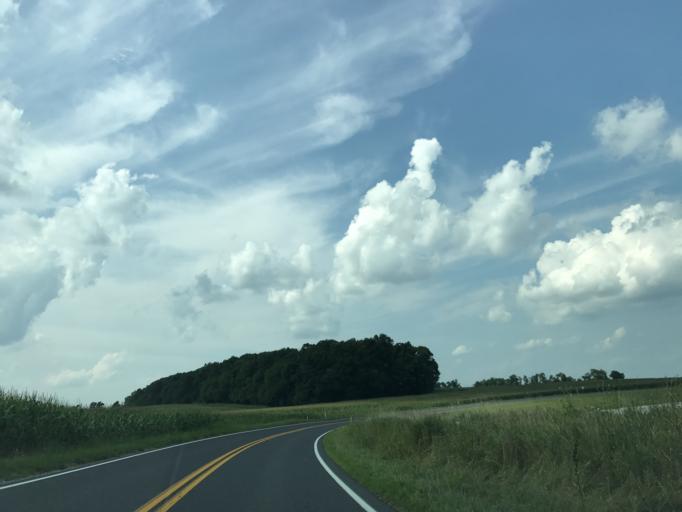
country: US
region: Pennsylvania
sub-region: York County
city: Pennville
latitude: 39.7511
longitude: -77.0011
